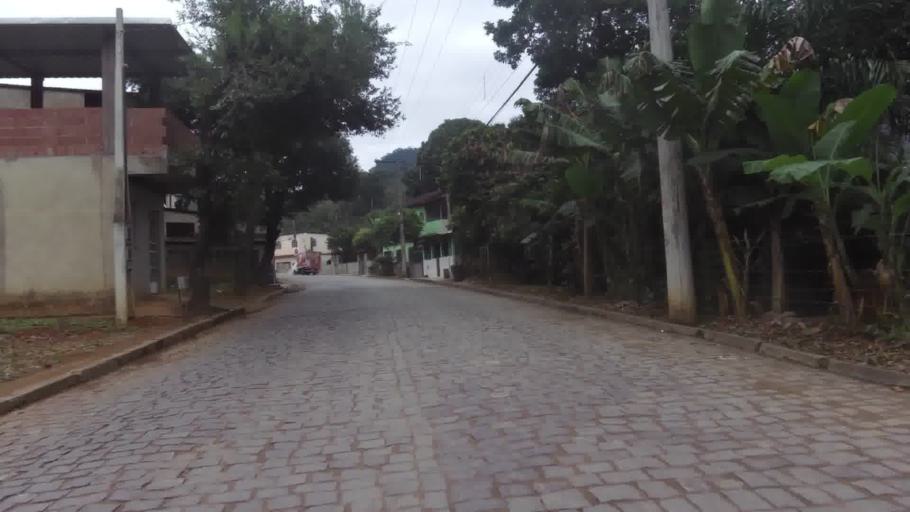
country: BR
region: Espirito Santo
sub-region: Iconha
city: Iconha
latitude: -20.7657
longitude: -40.8337
